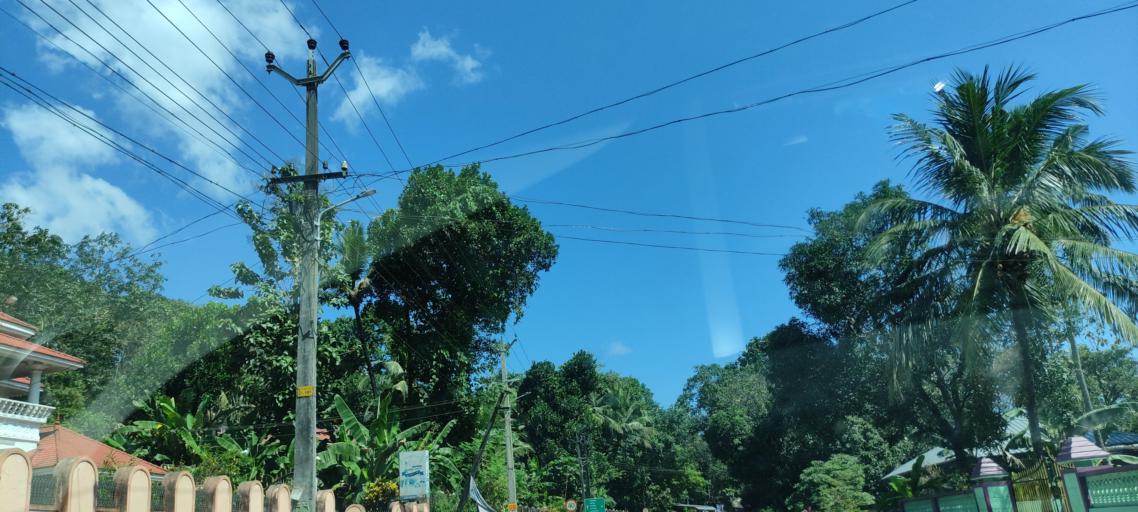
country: IN
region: Kerala
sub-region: Pattanamtitta
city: Adur
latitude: 9.1070
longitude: 76.6909
